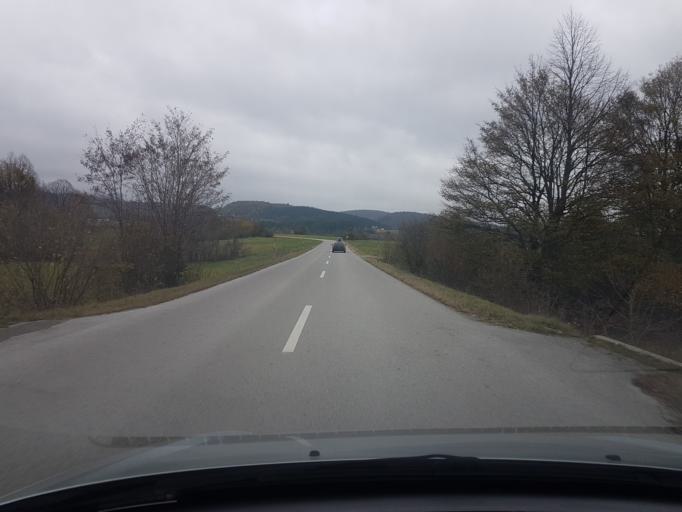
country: SI
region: Divaca
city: Divaca
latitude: 45.7246
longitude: 14.0037
